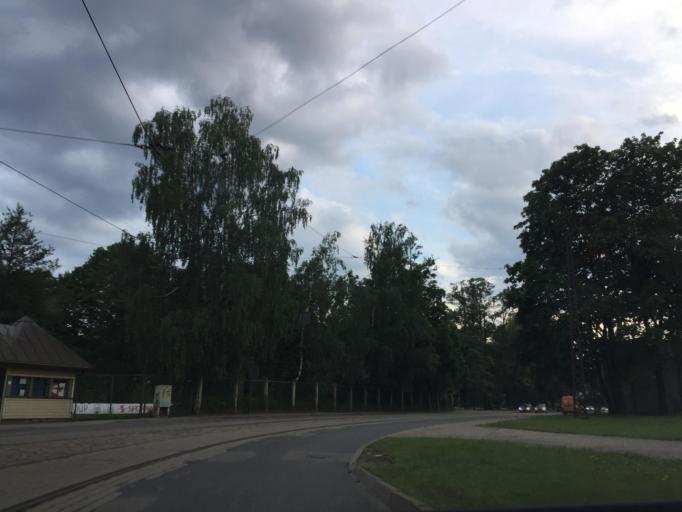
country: LV
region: Riga
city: Riga
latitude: 56.9341
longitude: 24.0869
